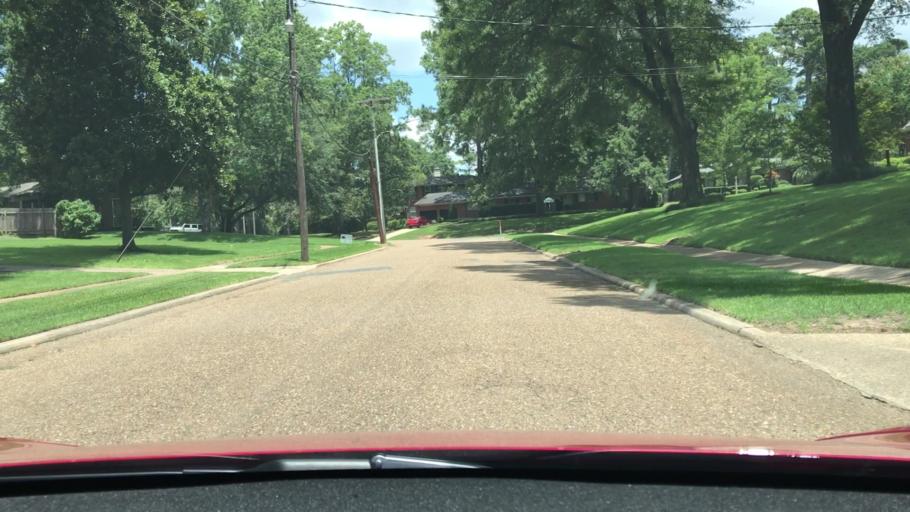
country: US
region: Louisiana
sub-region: Bossier Parish
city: Bossier City
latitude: 32.4583
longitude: -93.7538
